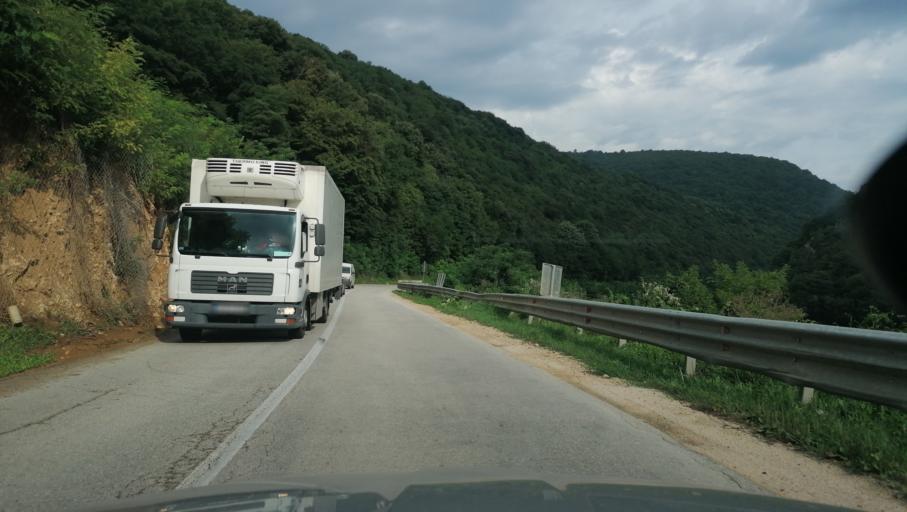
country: BA
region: Republika Srpska
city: Mrkonjic Grad
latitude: 44.5404
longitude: 17.1481
